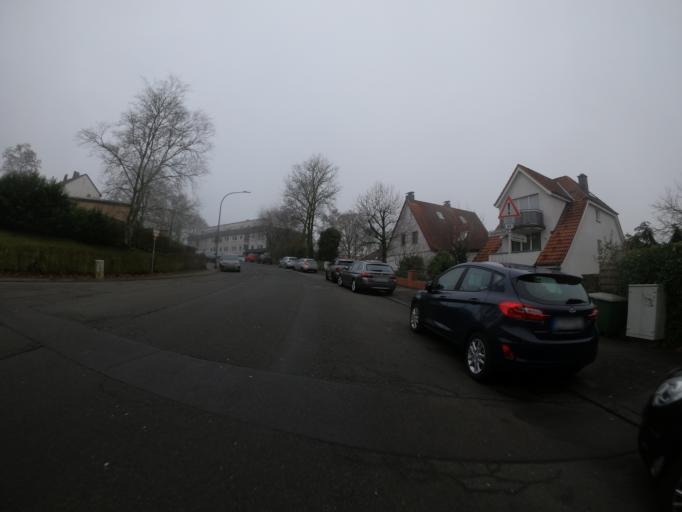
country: DE
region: North Rhine-Westphalia
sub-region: Regierungsbezirk Dusseldorf
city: Wuppertal
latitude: 51.2465
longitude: 7.1548
